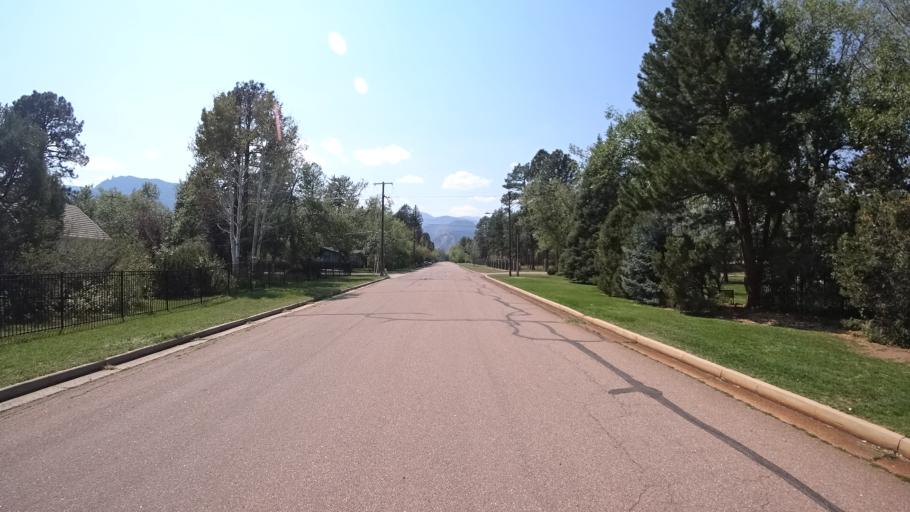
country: US
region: Colorado
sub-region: El Paso County
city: Colorado Springs
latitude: 38.7942
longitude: -104.8419
